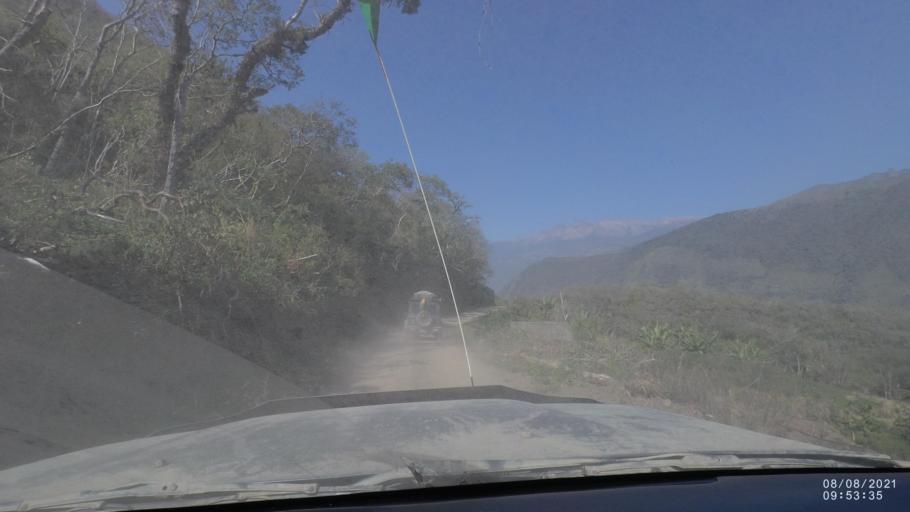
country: BO
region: La Paz
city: Quime
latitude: -16.6292
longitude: -66.7334
